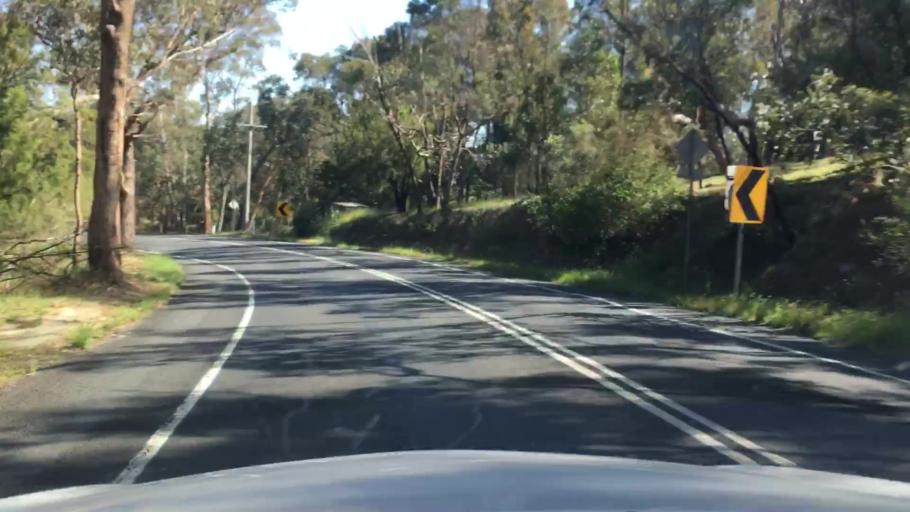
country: AU
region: Victoria
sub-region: Nillumbik
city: North Warrandyte
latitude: -37.7189
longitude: 145.2244
